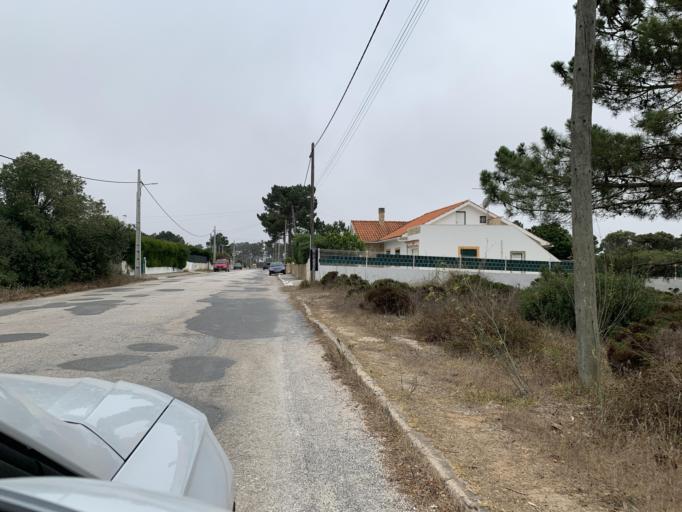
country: PT
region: Faro
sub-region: Aljezur
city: Aljezur
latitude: 37.3074
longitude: -8.8523
